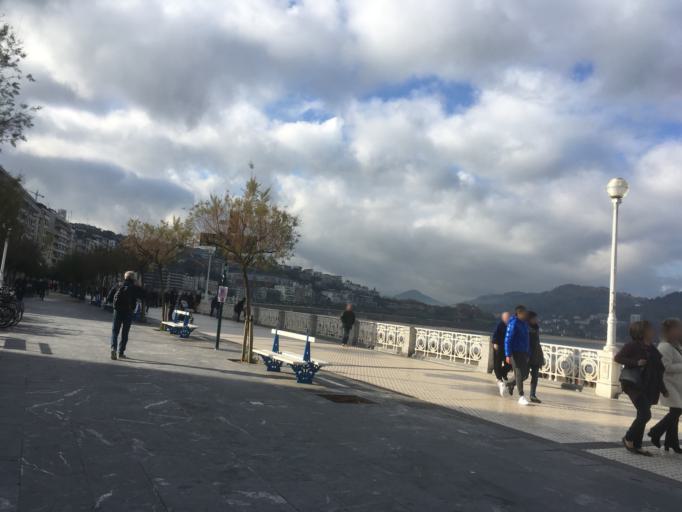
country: ES
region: Basque Country
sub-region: Provincia de Guipuzcoa
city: San Sebastian
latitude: 43.3188
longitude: -1.9850
